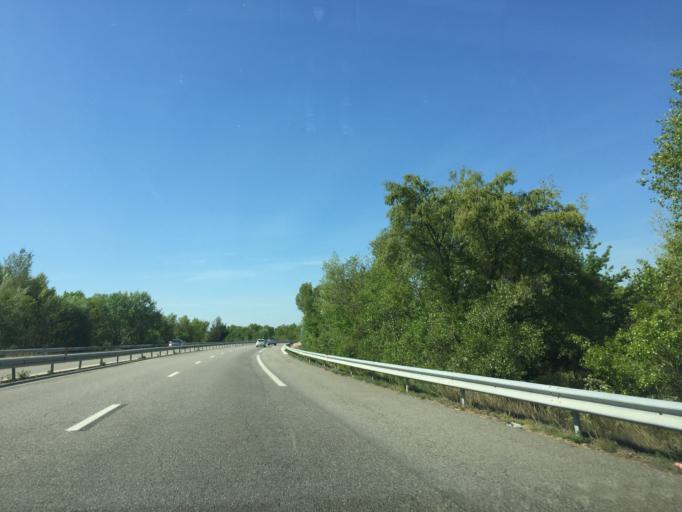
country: FR
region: Provence-Alpes-Cote d'Azur
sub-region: Departement des Alpes-de-Haute-Provence
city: Volx
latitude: 43.8537
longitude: 5.8599
